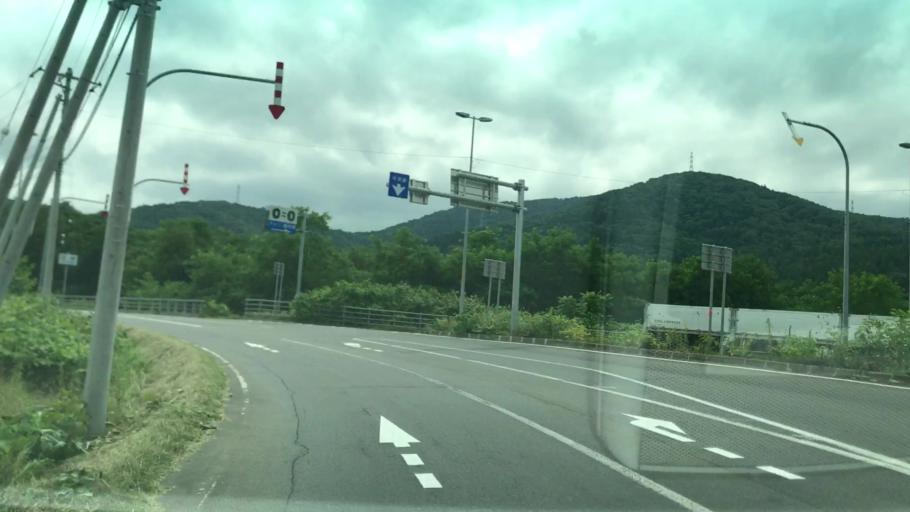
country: JP
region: Hokkaido
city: Yoichi
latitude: 43.0501
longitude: 140.8443
